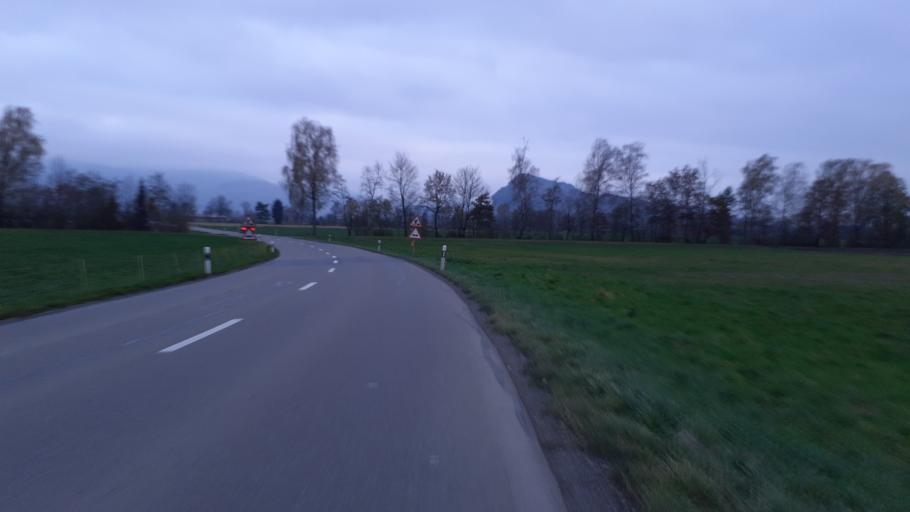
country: AT
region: Vorarlberg
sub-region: Politischer Bezirk Feldkirch
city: Mader
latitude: 47.3638
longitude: 9.5933
